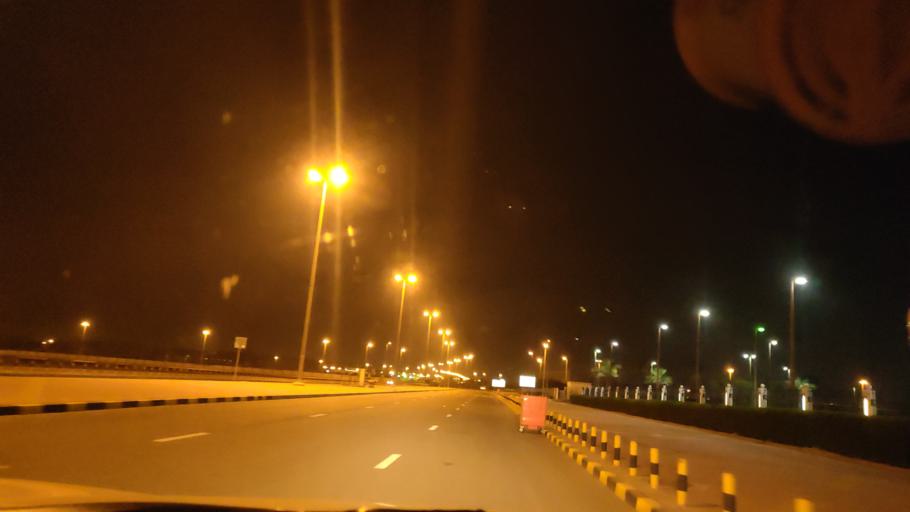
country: KW
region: Al Asimah
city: Ar Rabiyah
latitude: 29.2717
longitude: 47.9161
